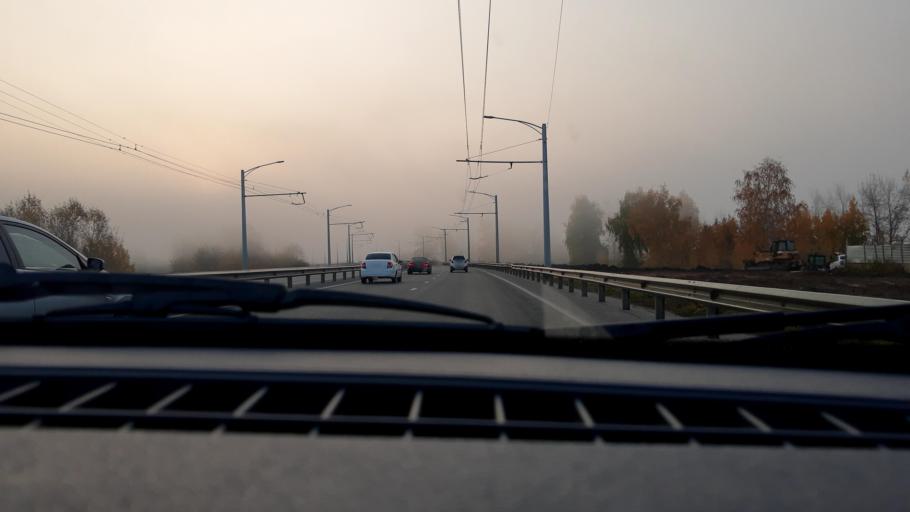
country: RU
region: Bashkortostan
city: Mikhaylovka
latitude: 54.7714
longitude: 55.9036
